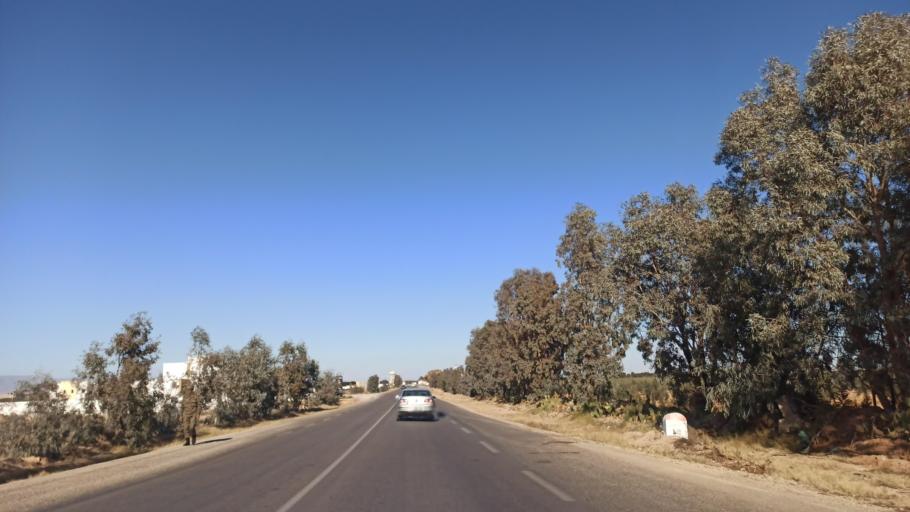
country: TN
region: Sidi Bu Zayd
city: Jilma
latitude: 35.1409
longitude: 9.3616
